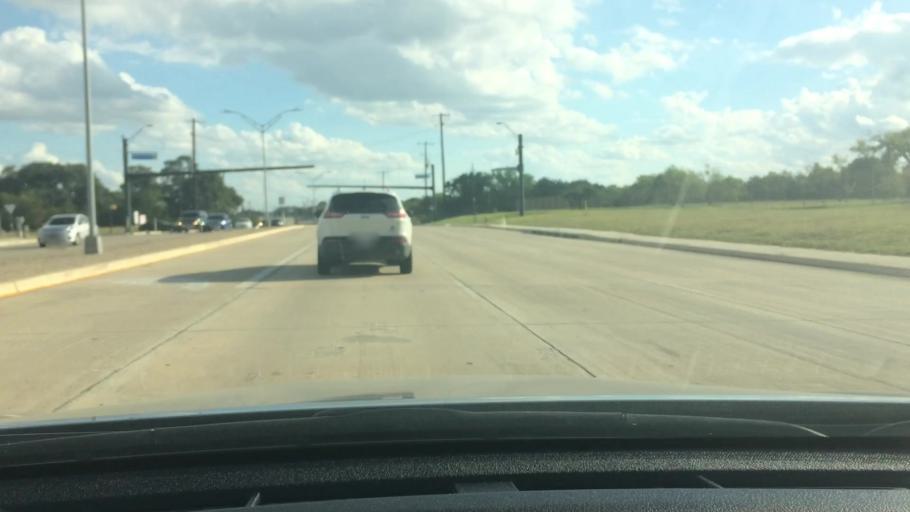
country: US
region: Texas
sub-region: Bexar County
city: Hollywood Park
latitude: 29.6172
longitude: -98.4226
